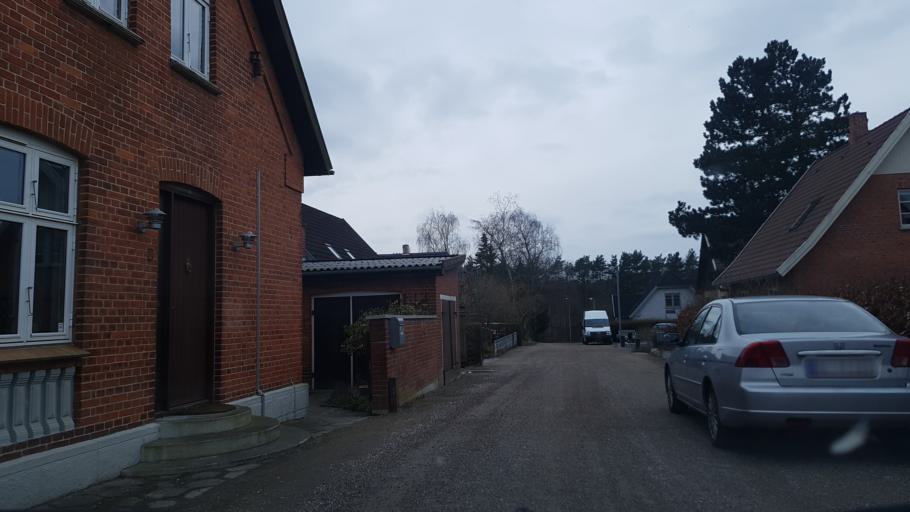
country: DK
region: Zealand
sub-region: Soro Kommune
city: Frederiksberg
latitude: 55.4174
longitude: 11.5666
